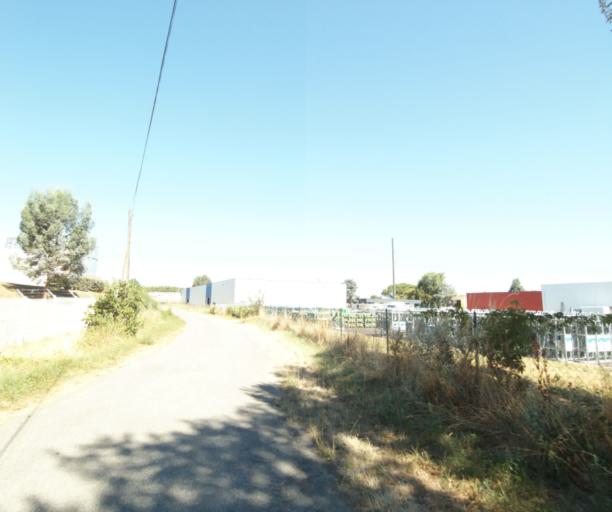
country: FR
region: Midi-Pyrenees
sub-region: Departement de la Haute-Garonne
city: Pechabou
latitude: 43.5106
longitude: 1.5236
